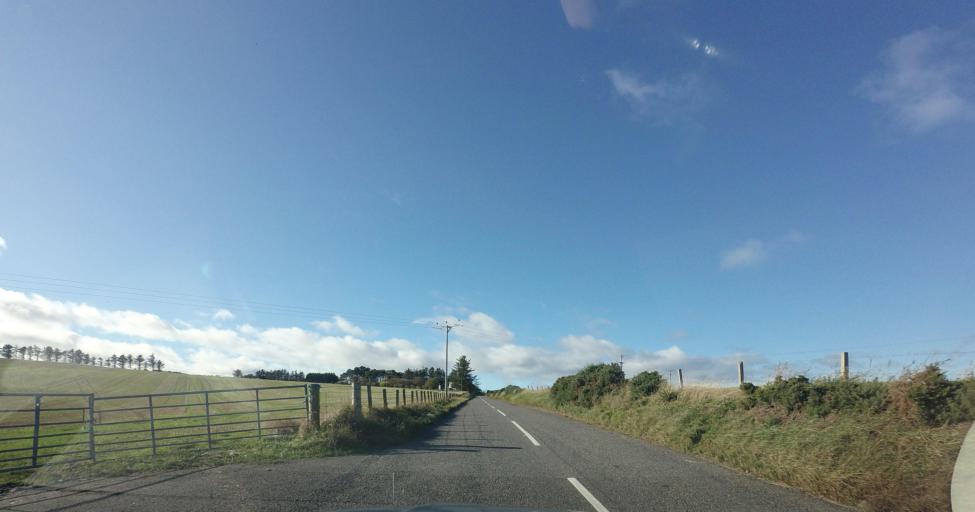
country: GB
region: Scotland
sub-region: Aberdeenshire
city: Rosehearty
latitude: 57.6778
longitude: -2.2839
